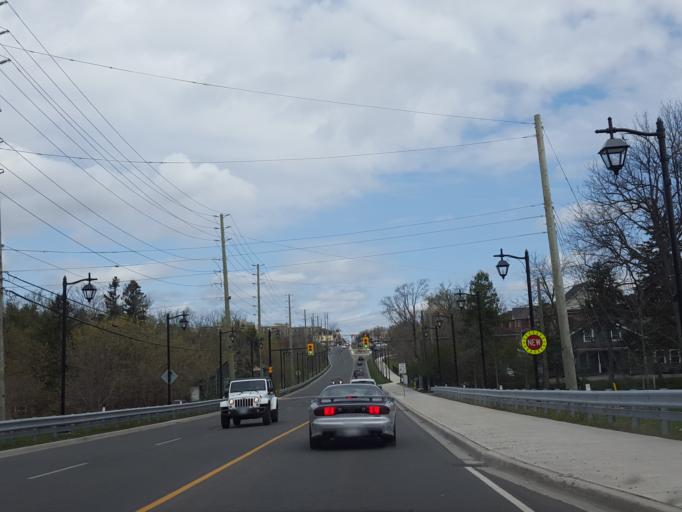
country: CA
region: Ontario
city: Markham
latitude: 43.8690
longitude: -79.2587
